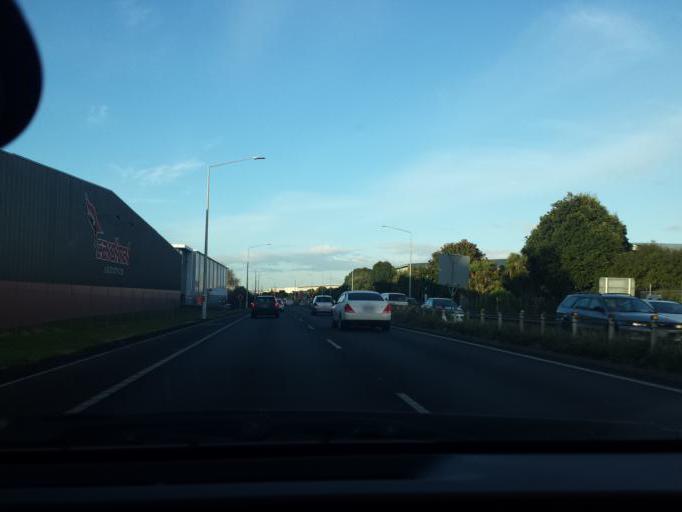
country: NZ
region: Auckland
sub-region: Auckland
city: Mangere
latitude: -36.9789
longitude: 174.7861
